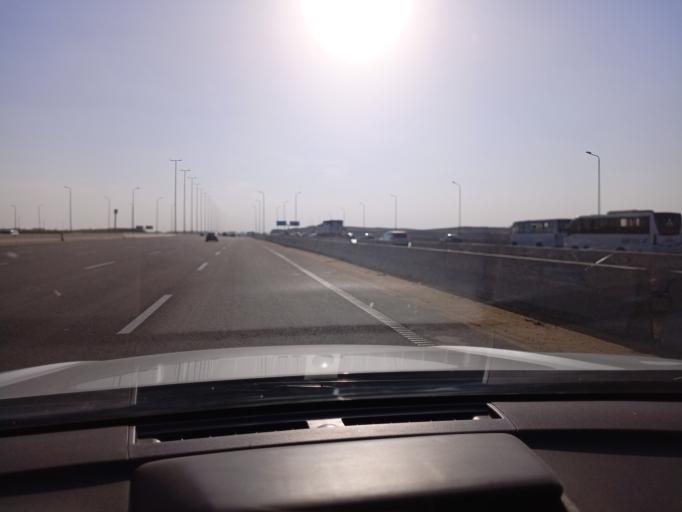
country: EG
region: Muhafazat al Qalyubiyah
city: Al Khankah
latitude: 30.0858
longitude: 31.4554
